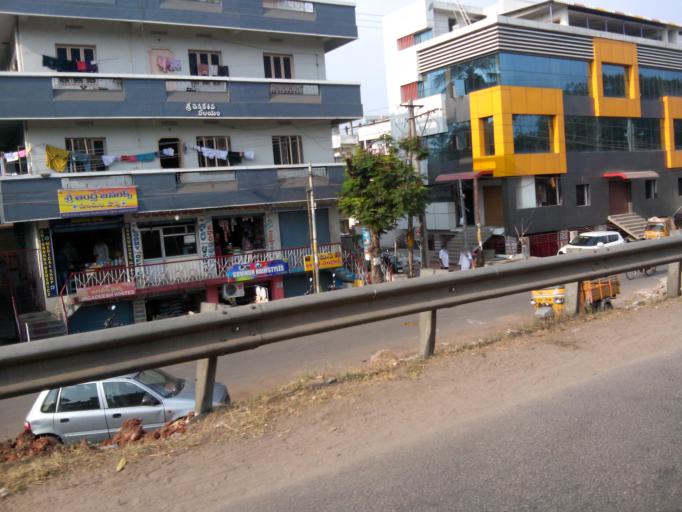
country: IN
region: Andhra Pradesh
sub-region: Krishna
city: Vijayawada
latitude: 16.5057
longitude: 80.6277
